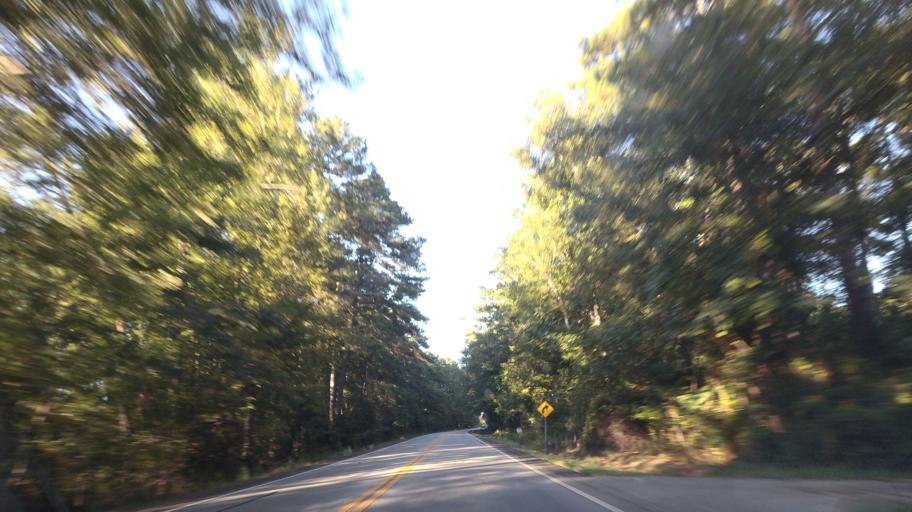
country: US
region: Georgia
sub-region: Spalding County
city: East Griffin
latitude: 33.2746
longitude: -84.2055
